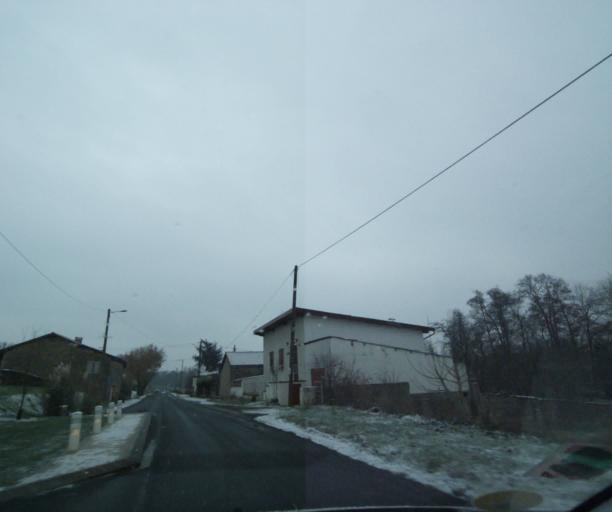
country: FR
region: Champagne-Ardenne
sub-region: Departement de la Haute-Marne
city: Wassy
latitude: 48.4479
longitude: 4.9571
